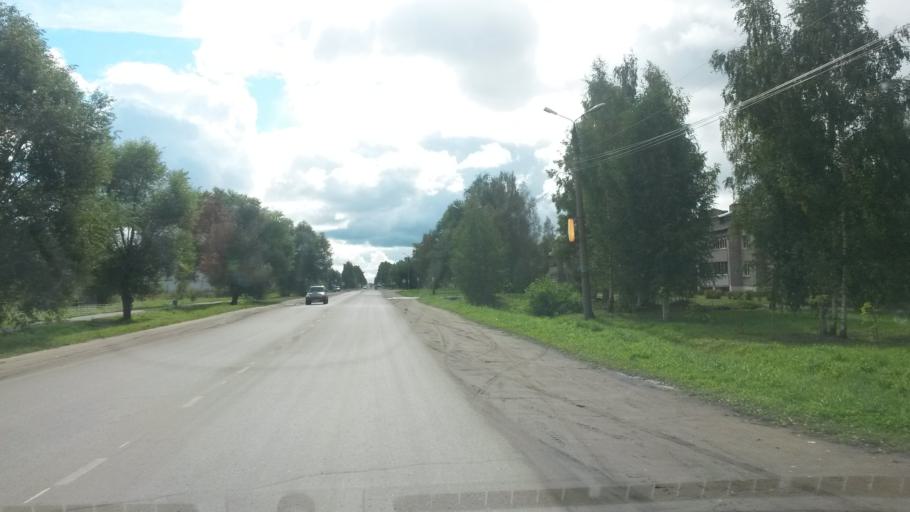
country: RU
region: Ivanovo
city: Zavolzhsk
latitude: 57.4838
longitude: 42.1457
